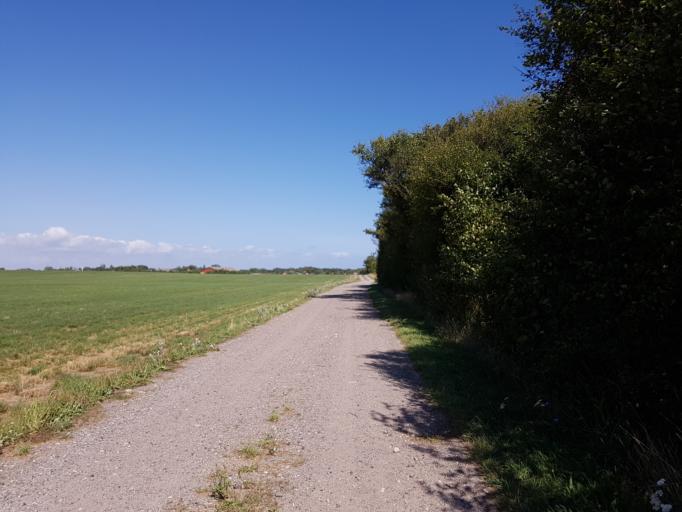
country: DK
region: Zealand
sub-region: Guldborgsund Kommune
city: Nykobing Falster
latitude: 54.5924
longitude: 11.9345
